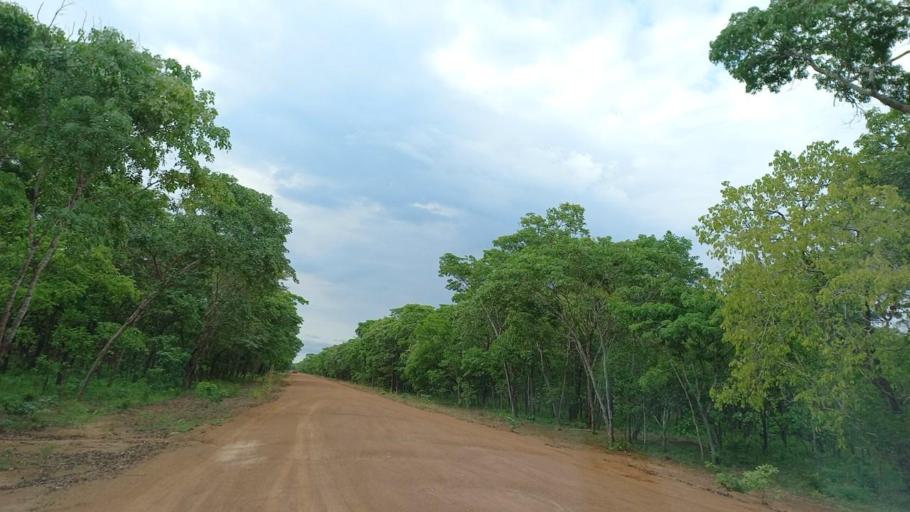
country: ZM
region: North-Western
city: Kalengwa
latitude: -13.3779
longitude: 25.0727
